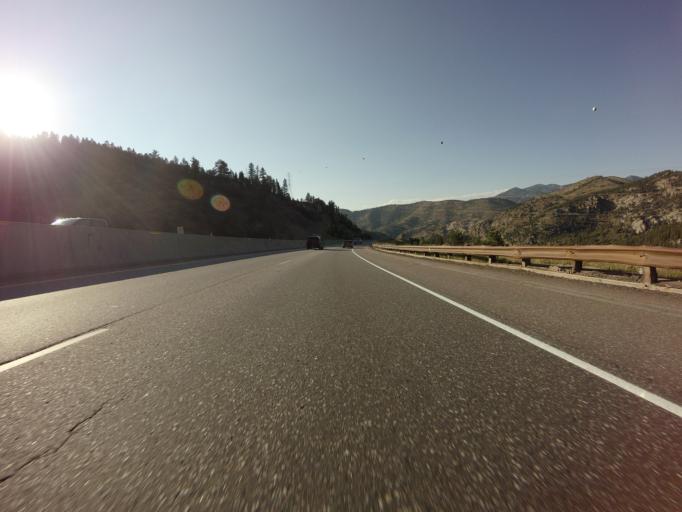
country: US
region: Colorado
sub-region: Clear Creek County
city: Idaho Springs
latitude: 39.7301
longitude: -105.4258
